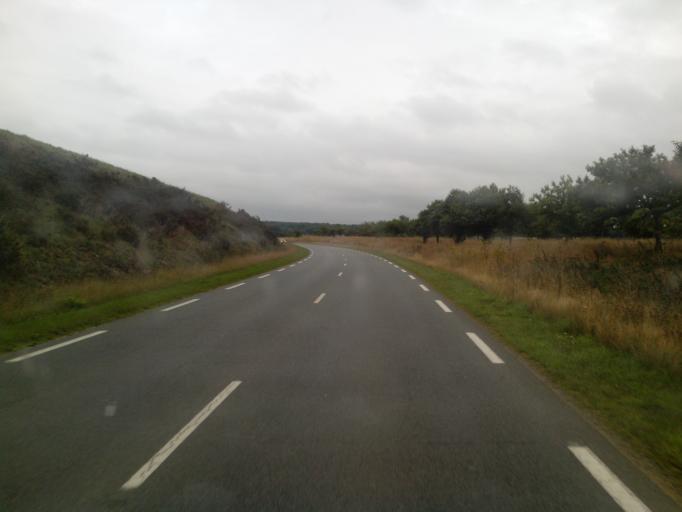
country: FR
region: Brittany
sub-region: Departement des Cotes-d'Armor
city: Lezardrieux
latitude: 48.7713
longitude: -3.0964
